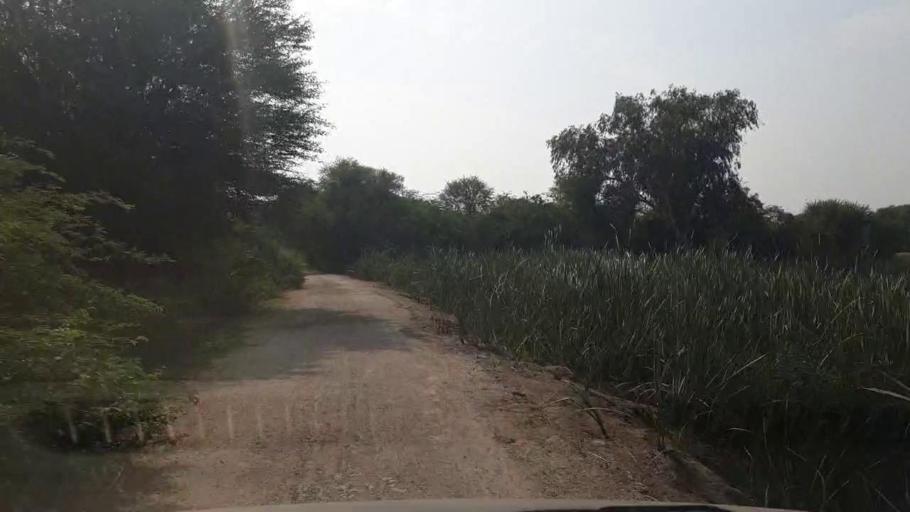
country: PK
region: Sindh
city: Tando Muhammad Khan
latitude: 25.1322
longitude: 68.4350
